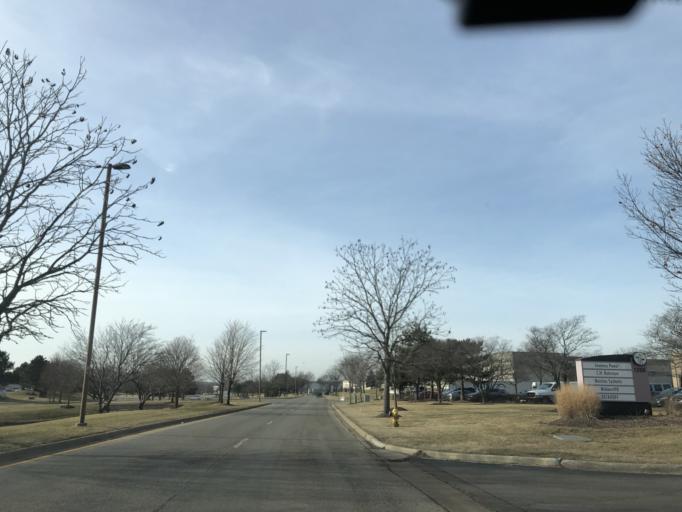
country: US
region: Illinois
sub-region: Cook County
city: Lemont
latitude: 41.6964
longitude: -88.0120
